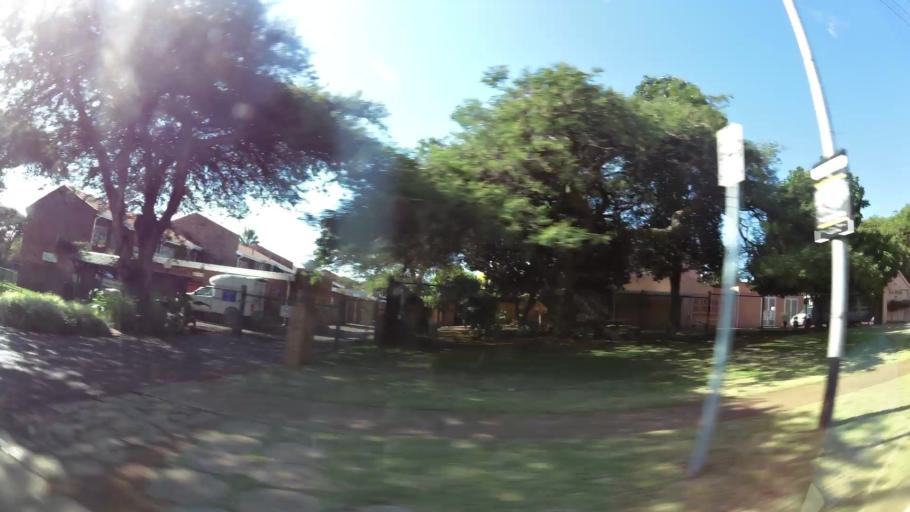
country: ZA
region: Gauteng
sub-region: City of Tshwane Metropolitan Municipality
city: Pretoria
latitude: -25.6839
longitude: 28.2157
